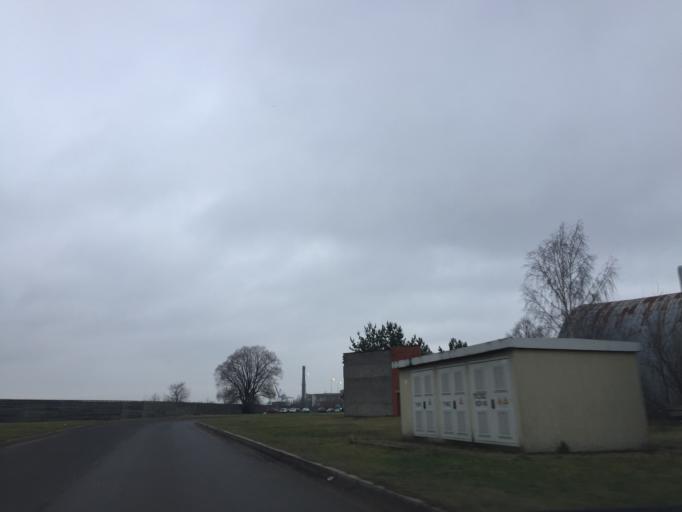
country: LV
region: Riga
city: Riga
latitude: 56.9904
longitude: 24.1128
